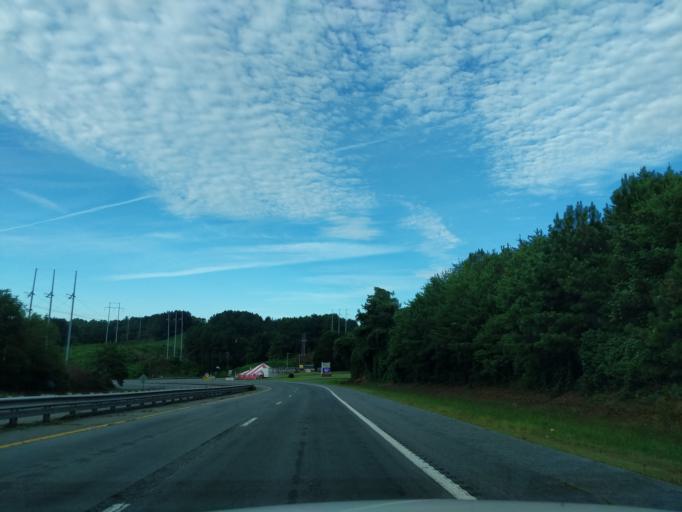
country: US
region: Georgia
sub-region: Fannin County
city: McCaysville
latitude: 35.0058
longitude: -84.3867
